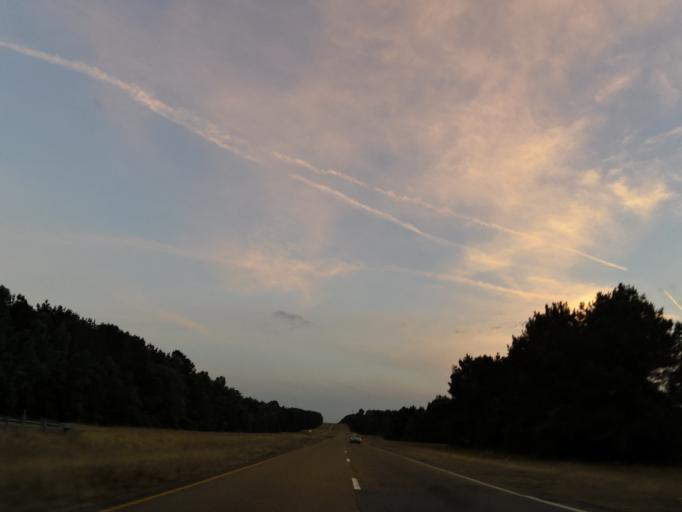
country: US
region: Mississippi
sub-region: Lauderdale County
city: Meridian Station
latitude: 32.6461
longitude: -88.4954
